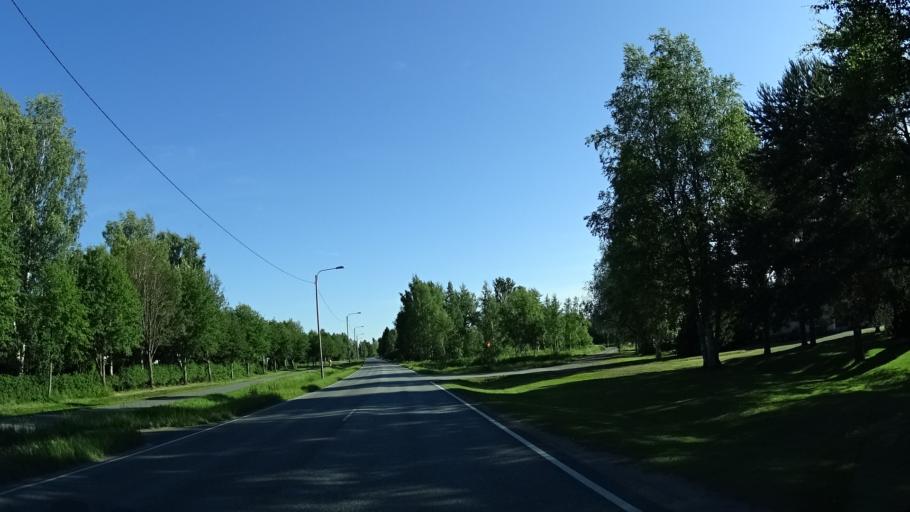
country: FI
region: Satakunta
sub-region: Pori
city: Ulvila
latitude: 61.4542
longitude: 21.8930
